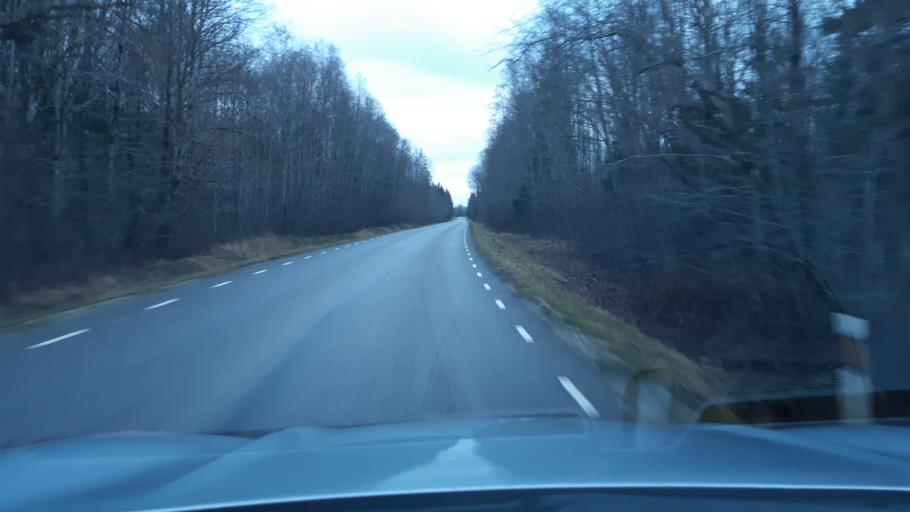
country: EE
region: Raplamaa
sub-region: Kohila vald
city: Kohila
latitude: 59.1112
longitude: 24.6833
